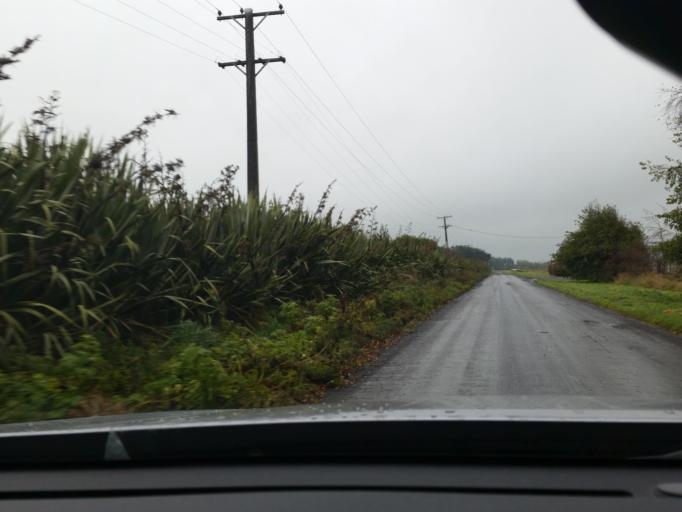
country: NZ
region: Southland
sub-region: Invercargill City
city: Invercargill
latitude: -46.3032
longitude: 168.3033
